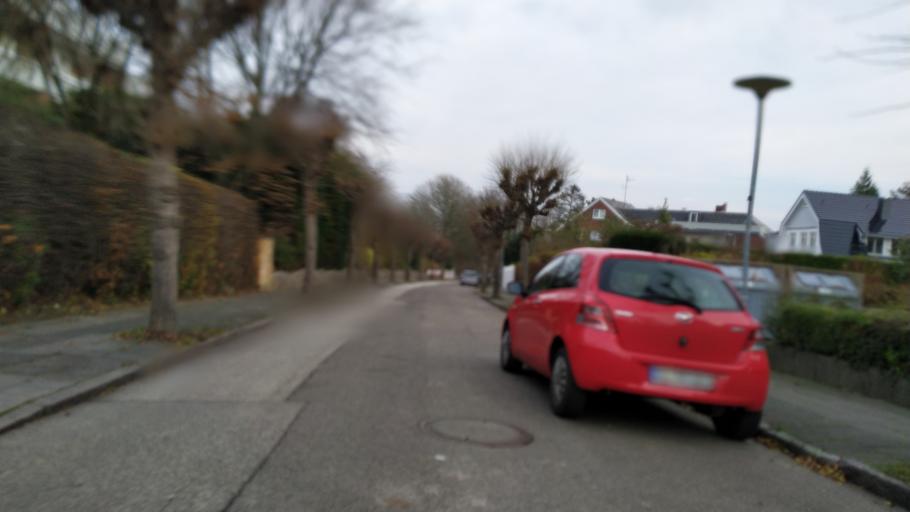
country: DE
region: Schleswig-Holstein
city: Travemuende
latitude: 53.9697
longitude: 10.8773
